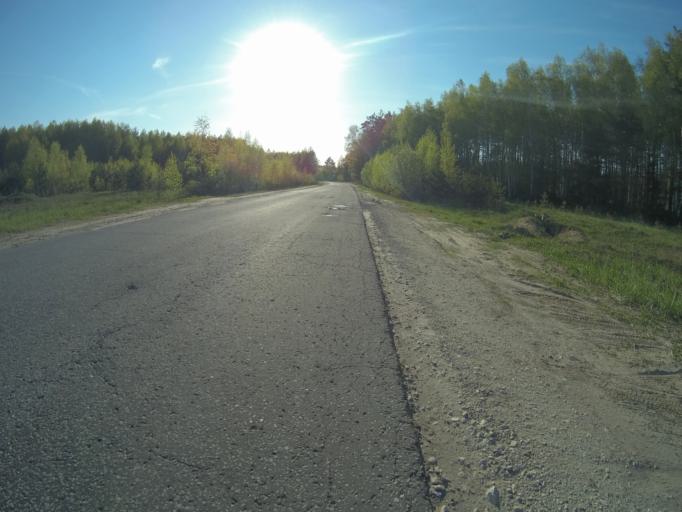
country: RU
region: Vladimir
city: Sudogda
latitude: 56.1024
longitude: 40.7801
